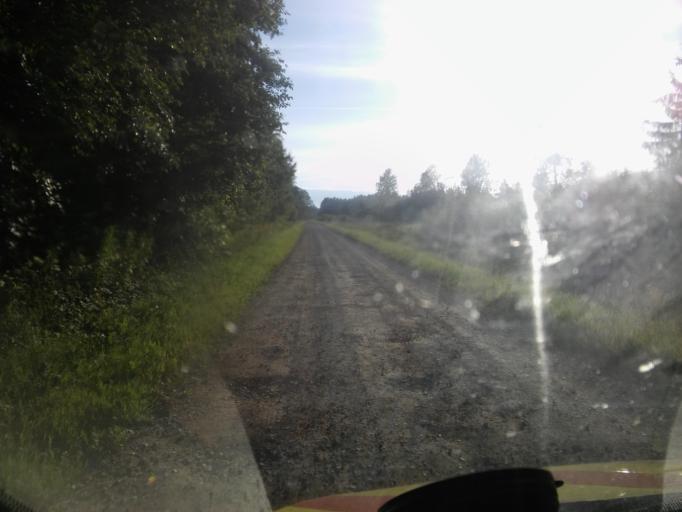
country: EE
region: Valgamaa
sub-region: Torva linn
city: Torva
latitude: 58.0934
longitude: 25.9285
